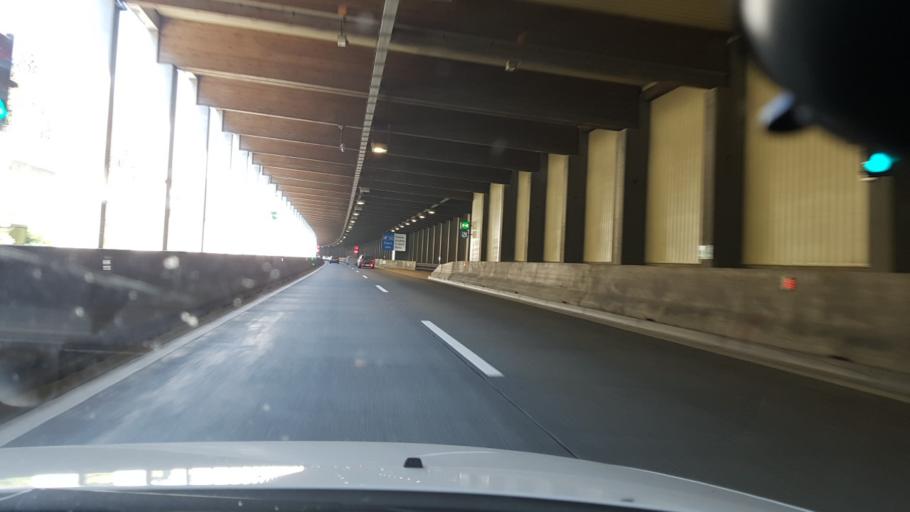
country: AT
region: Salzburg
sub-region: Politischer Bezirk Sankt Johann im Pongau
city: Eben im Pongau
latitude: 47.4054
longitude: 13.3938
